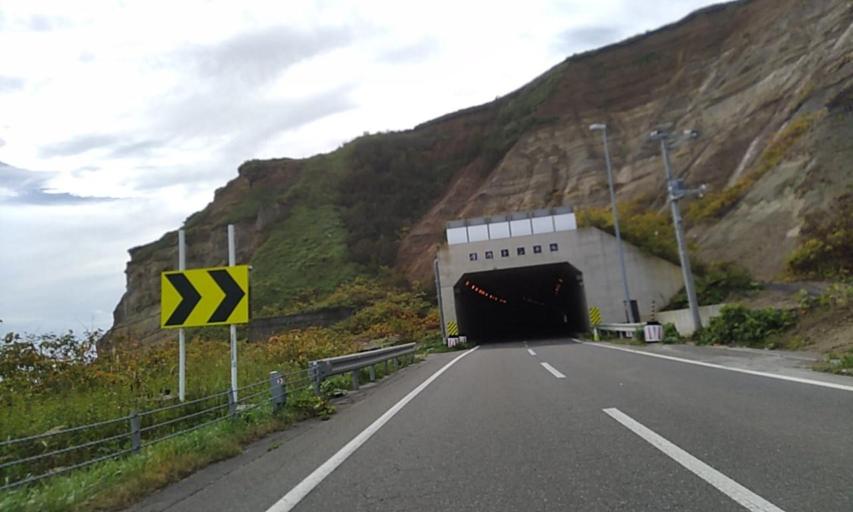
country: JP
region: Hokkaido
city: Obihiro
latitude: 42.7651
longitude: 143.7651
